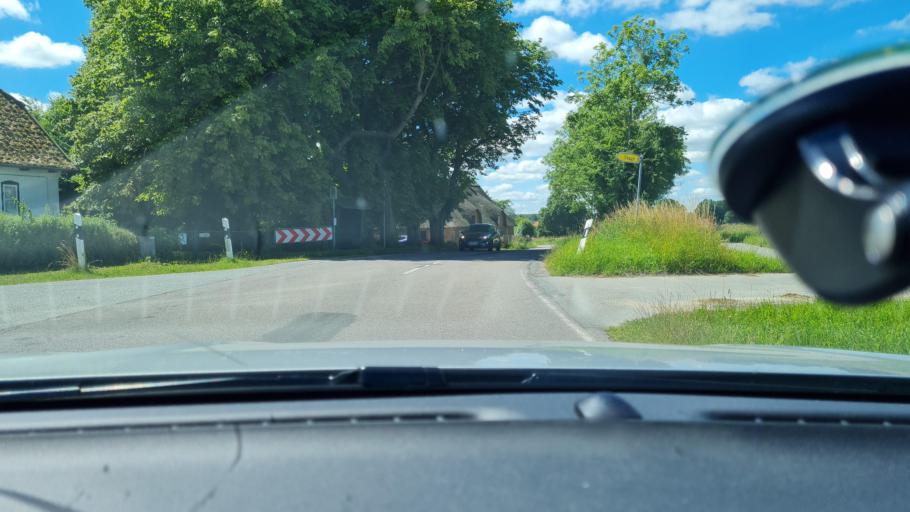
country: DE
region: Schleswig-Holstein
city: Thumby
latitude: 54.5984
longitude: 9.9134
